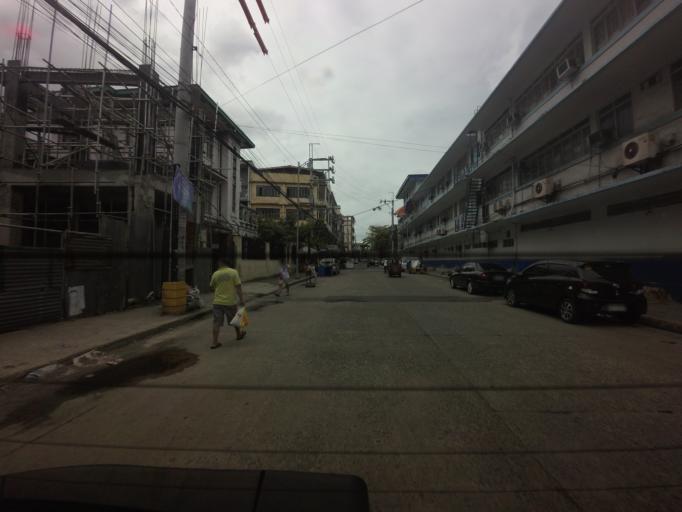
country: PH
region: Metro Manila
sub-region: City of Manila
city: Manila
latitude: 14.6088
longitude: 120.9665
